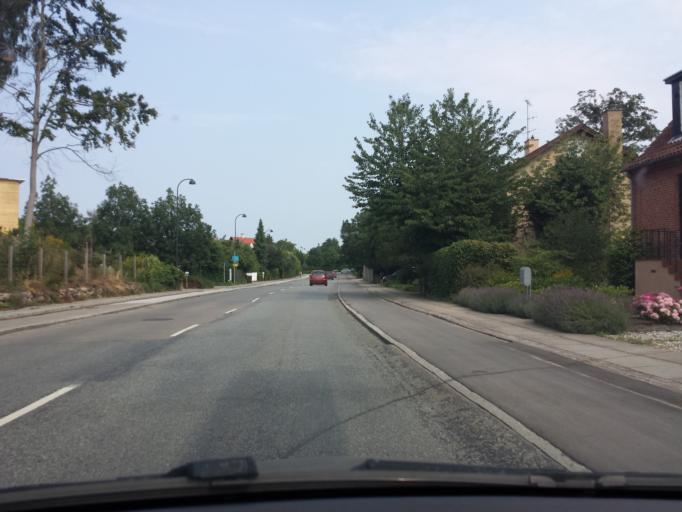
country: DK
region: Capital Region
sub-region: Gentofte Kommune
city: Charlottenlund
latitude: 55.7728
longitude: 12.5814
